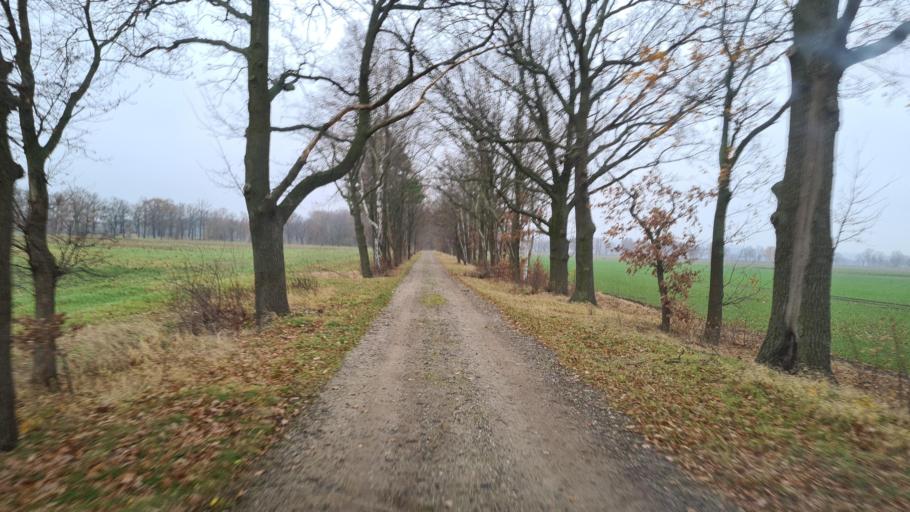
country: DE
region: Brandenburg
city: Schraden
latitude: 51.4101
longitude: 13.7063
